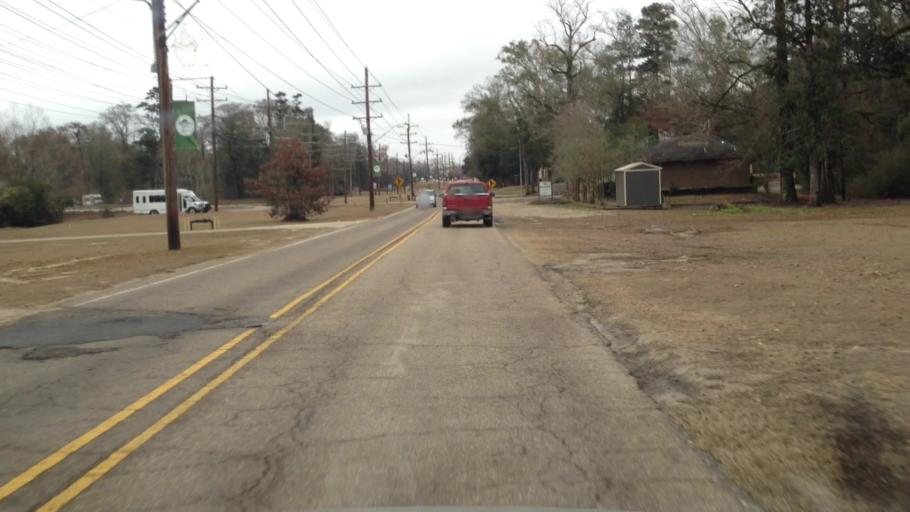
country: US
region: Louisiana
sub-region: Washington Parish
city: Bogalusa
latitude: 30.7823
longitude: -89.8718
